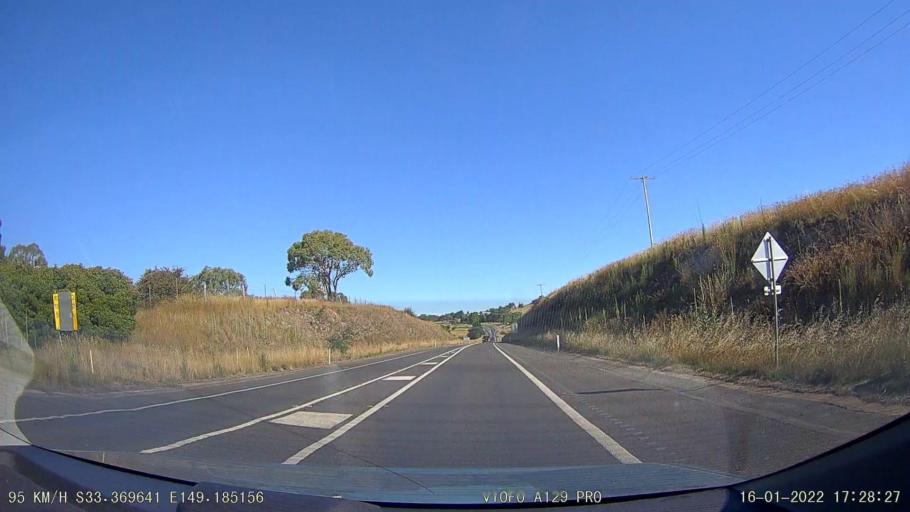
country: AU
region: New South Wales
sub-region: Blayney
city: Millthorpe
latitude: -33.3699
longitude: 149.1848
